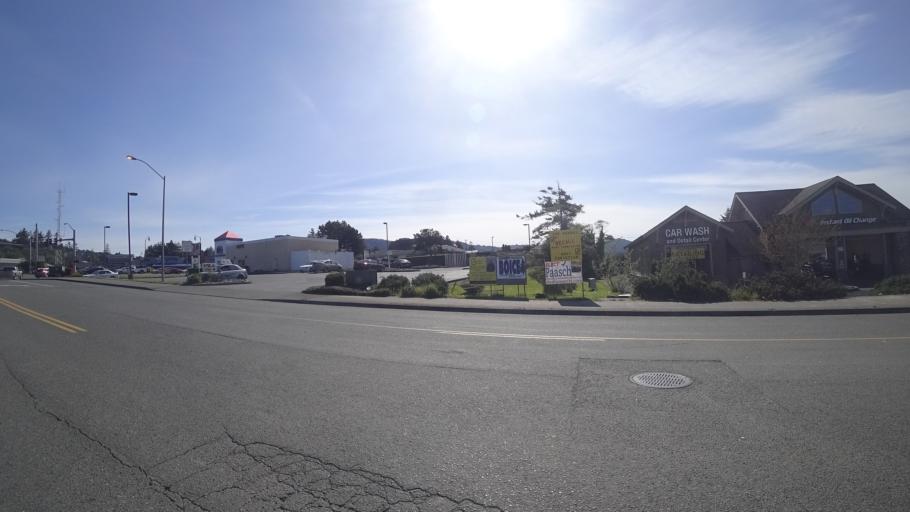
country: US
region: Oregon
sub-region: Curry County
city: Brookings
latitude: 42.0537
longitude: -124.2888
